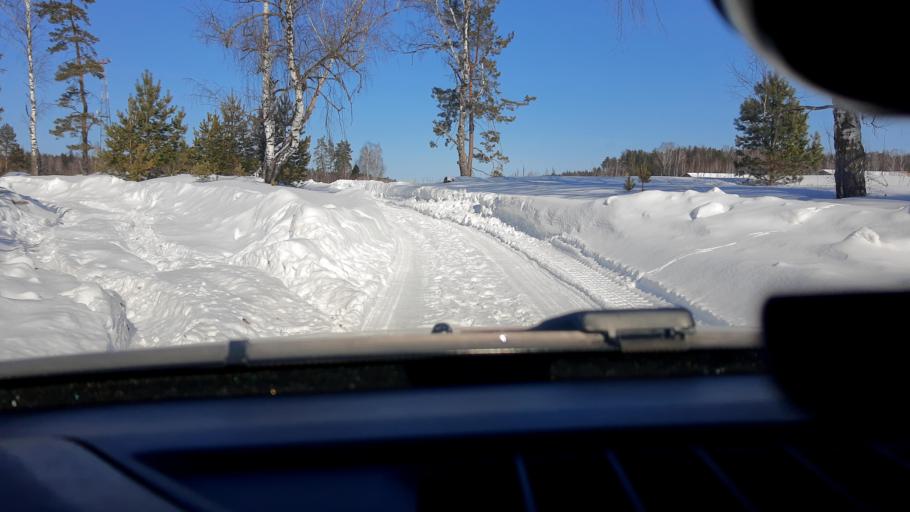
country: RU
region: Nizjnij Novgorod
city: Yuganets
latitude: 56.2567
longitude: 43.2272
